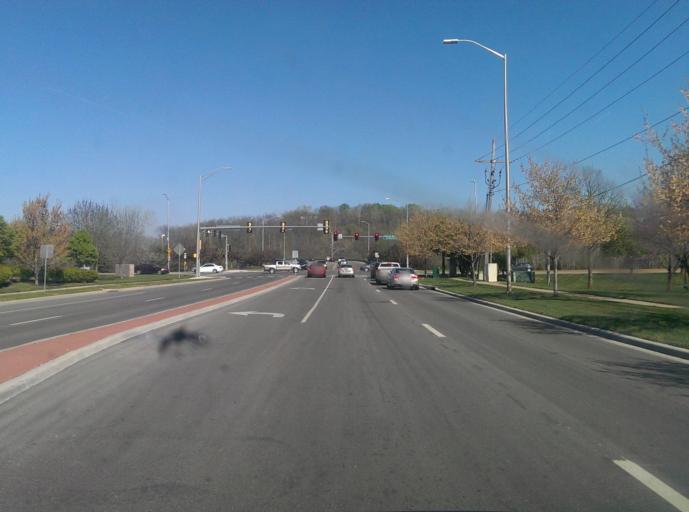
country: US
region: Kansas
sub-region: Johnson County
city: Leawood
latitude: 38.9275
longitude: -94.6263
